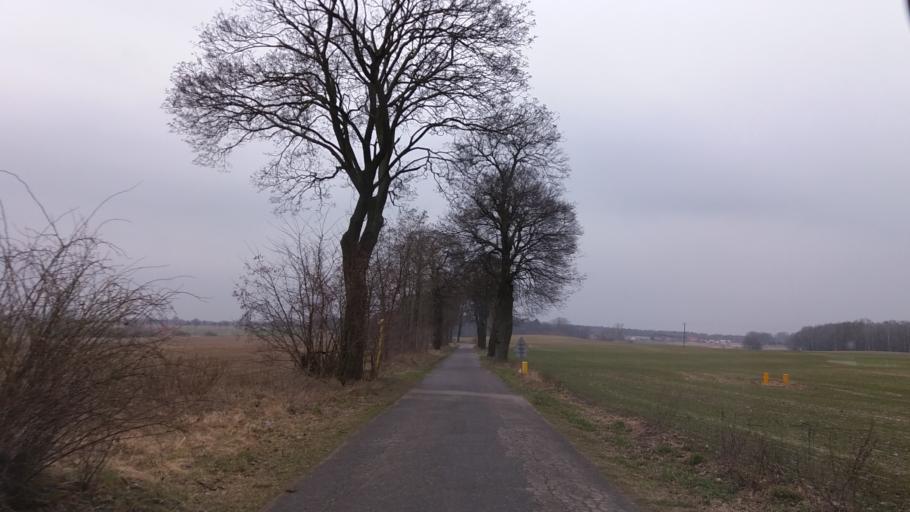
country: PL
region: West Pomeranian Voivodeship
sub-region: Powiat choszczenski
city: Choszczno
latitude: 53.1362
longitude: 15.3618
